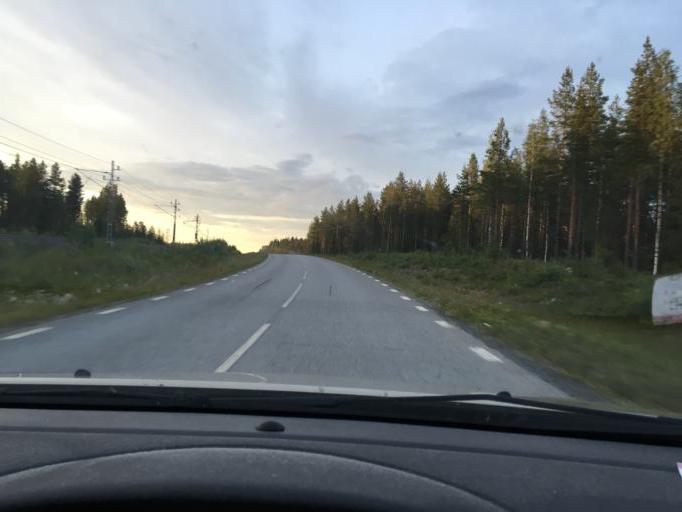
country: SE
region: Norrbotten
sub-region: Lulea Kommun
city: Ranea
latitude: 66.0405
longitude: 22.3355
